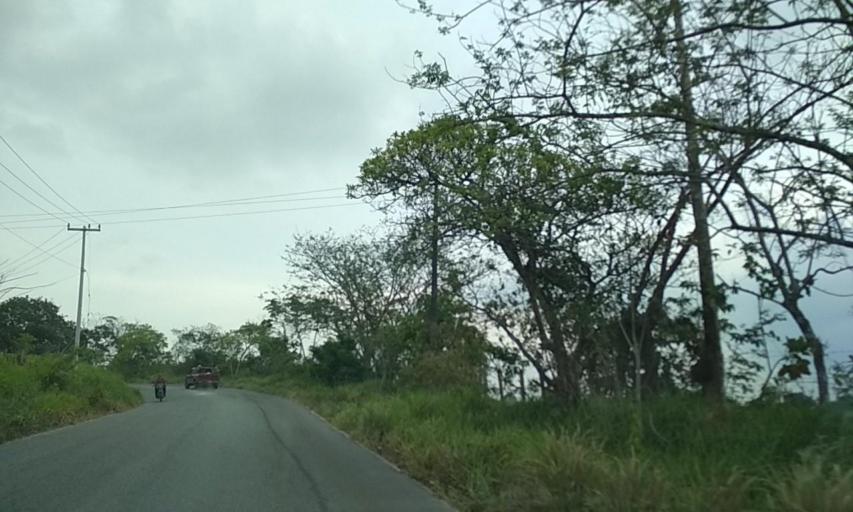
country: MX
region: Veracruz
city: Las Choapas
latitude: 17.8006
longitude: -94.1099
